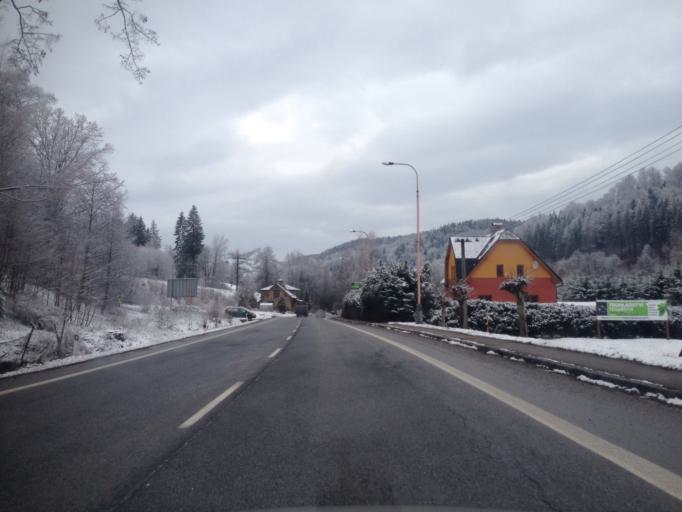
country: CZ
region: Liberecky
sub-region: Okres Semily
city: Ponikla
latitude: 50.6302
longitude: 15.4732
